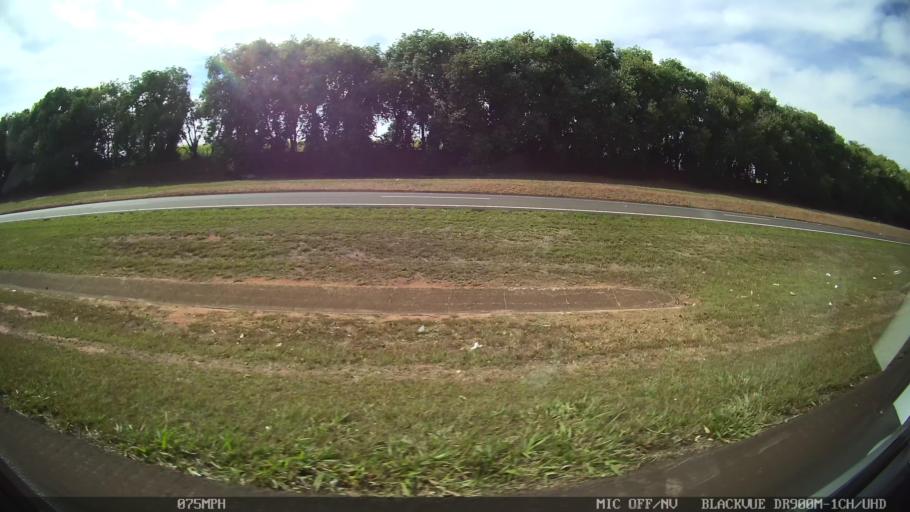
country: BR
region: Sao Paulo
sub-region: Matao
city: Matao
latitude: -21.6261
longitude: -48.4085
